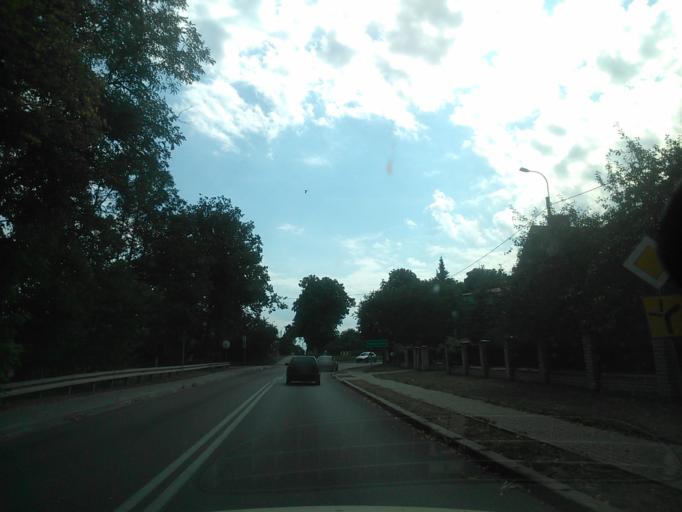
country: PL
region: Warmian-Masurian Voivodeship
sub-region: Powiat dzialdowski
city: Ilowo -Osada
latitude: 53.1749
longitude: 20.2975
